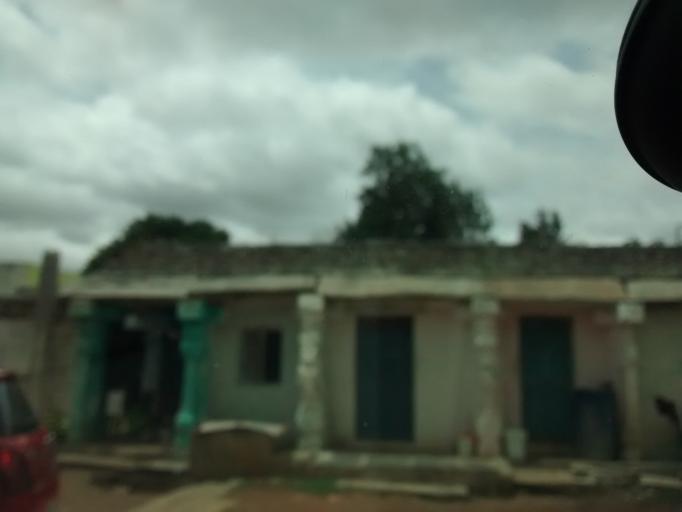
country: IN
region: Andhra Pradesh
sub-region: Anantapur
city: Hindupur
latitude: 13.8029
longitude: 77.6093
